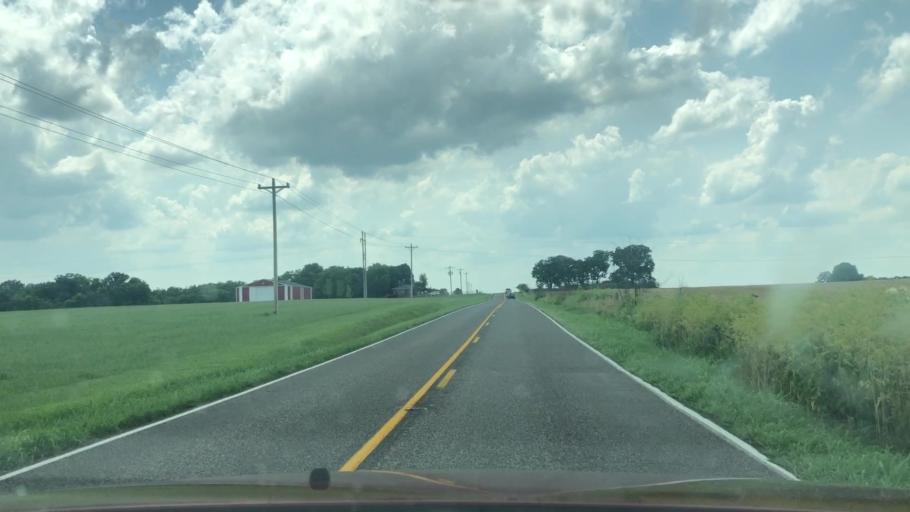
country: US
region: Missouri
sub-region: Christian County
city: Ozark
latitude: 36.9430
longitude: -93.2422
